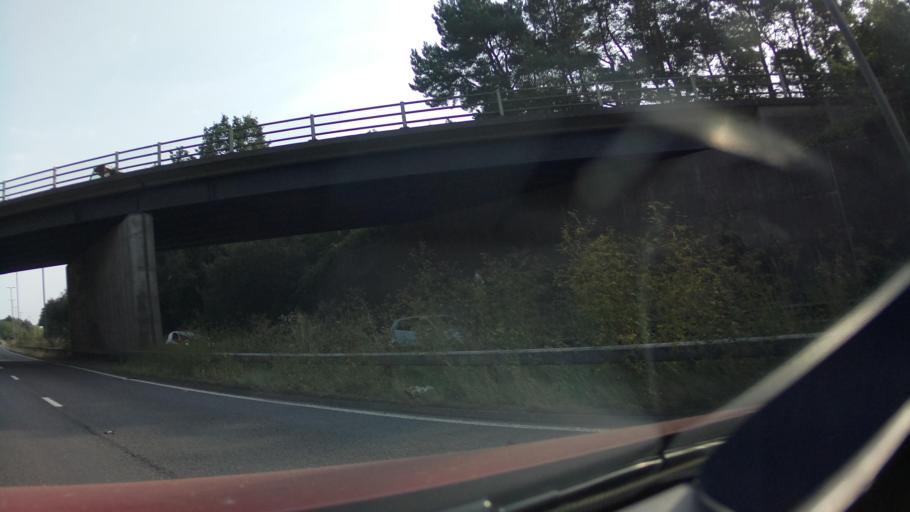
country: GB
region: England
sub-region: Solihull
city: Tidbury Green
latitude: 52.3464
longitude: -1.8777
